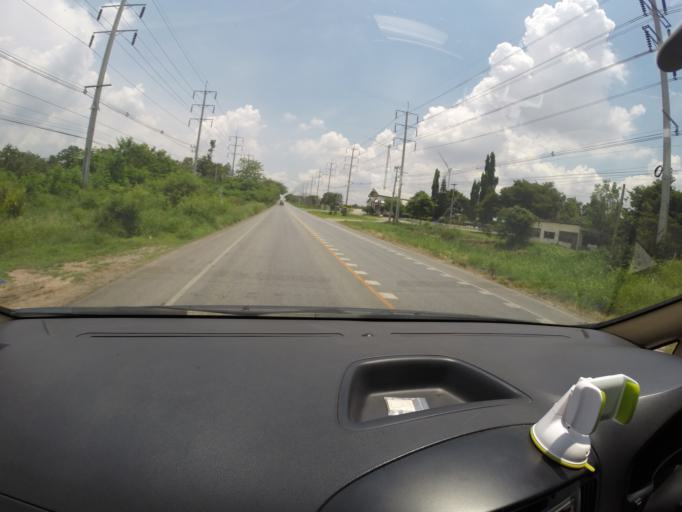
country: TH
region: Nakhon Ratchasima
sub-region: Amphoe Thepharak
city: Thepharak
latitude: 15.1192
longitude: 101.4900
